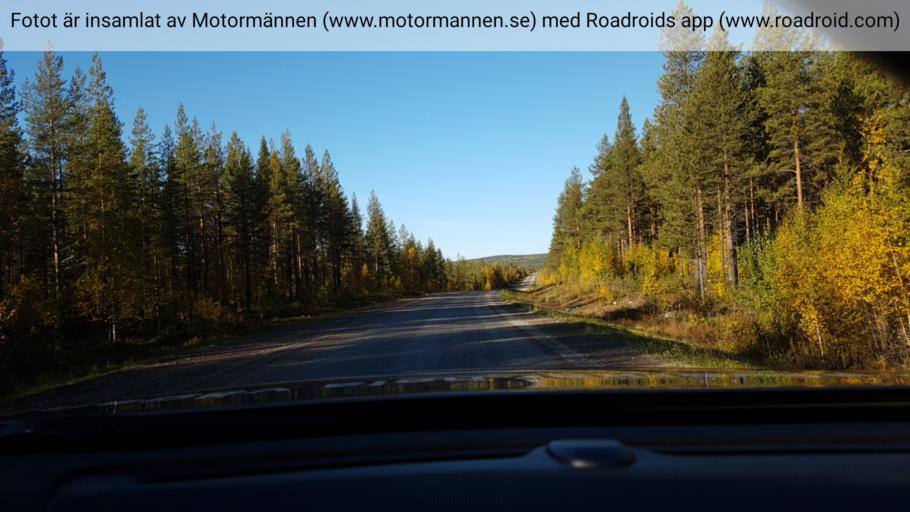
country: SE
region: Norrbotten
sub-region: Alvsbyns Kommun
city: AElvsbyn
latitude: 66.2648
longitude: 21.0427
